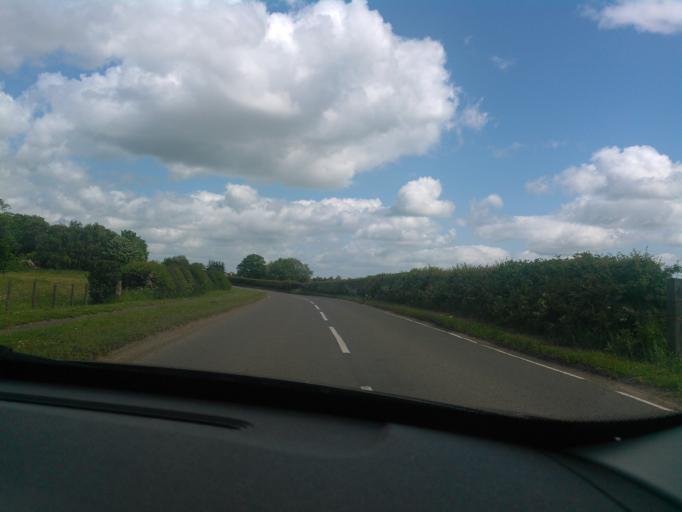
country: GB
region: England
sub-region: Shropshire
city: Wem
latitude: 52.8611
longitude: -2.7037
